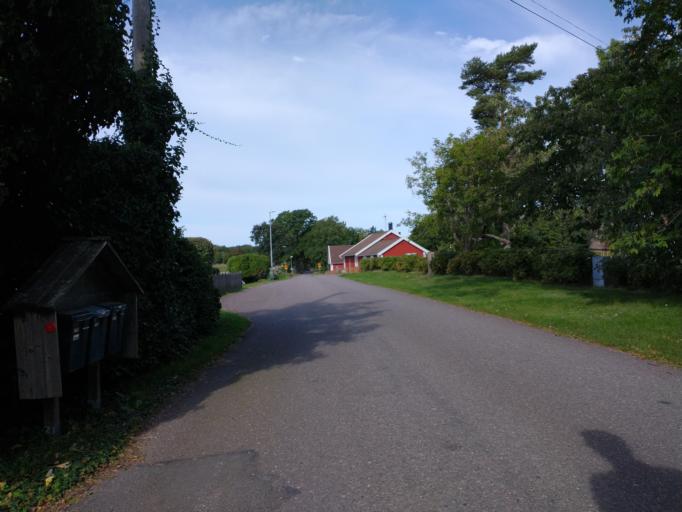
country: SE
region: Kalmar
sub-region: Kalmar Kommun
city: Lindsdal
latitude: 56.7786
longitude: 16.3063
